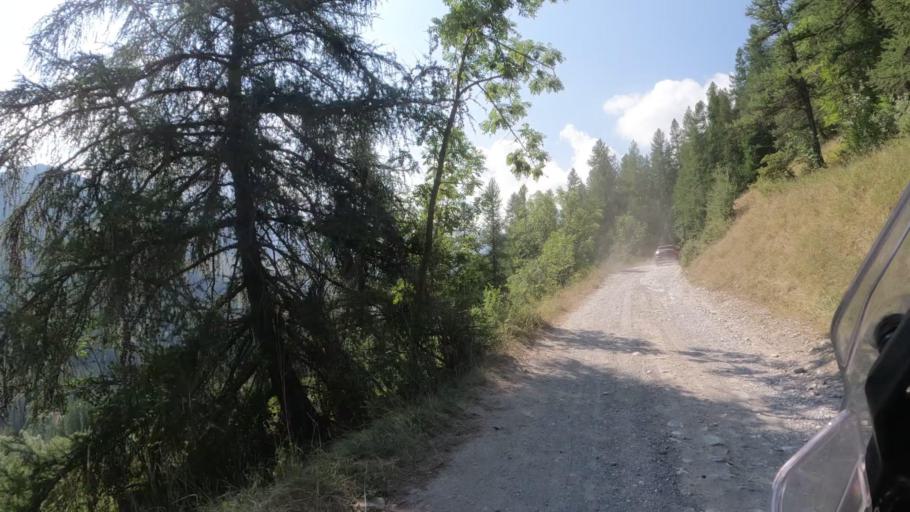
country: IT
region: Piedmont
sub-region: Provincia di Torino
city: Cesana Torinese
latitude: 44.9292
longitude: 6.8134
